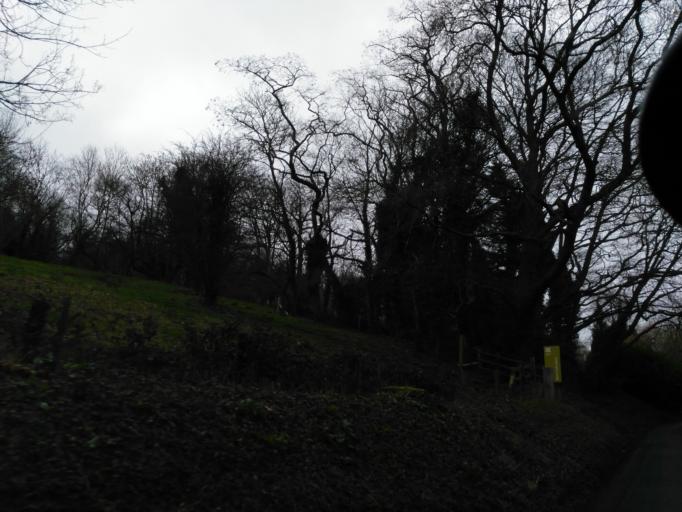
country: GB
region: England
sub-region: Bath and North East Somerset
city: Bath
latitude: 51.3829
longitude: -2.3406
